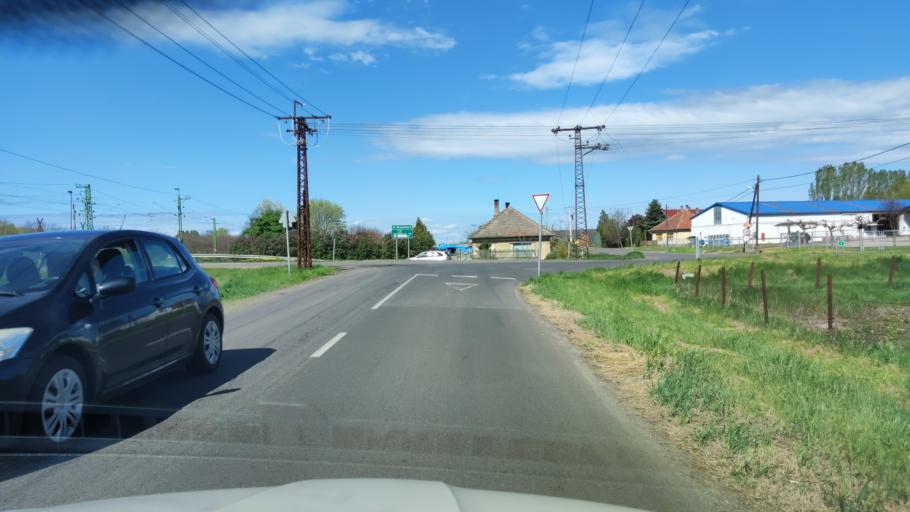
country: HU
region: Pest
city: Abony
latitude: 47.1728
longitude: 20.0052
